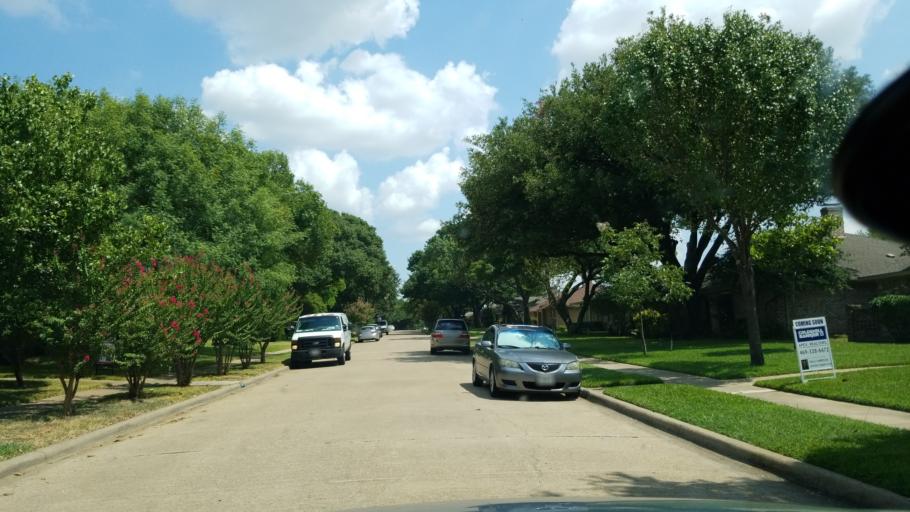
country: US
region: Texas
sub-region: Dallas County
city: Richardson
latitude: 32.9269
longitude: -96.7264
